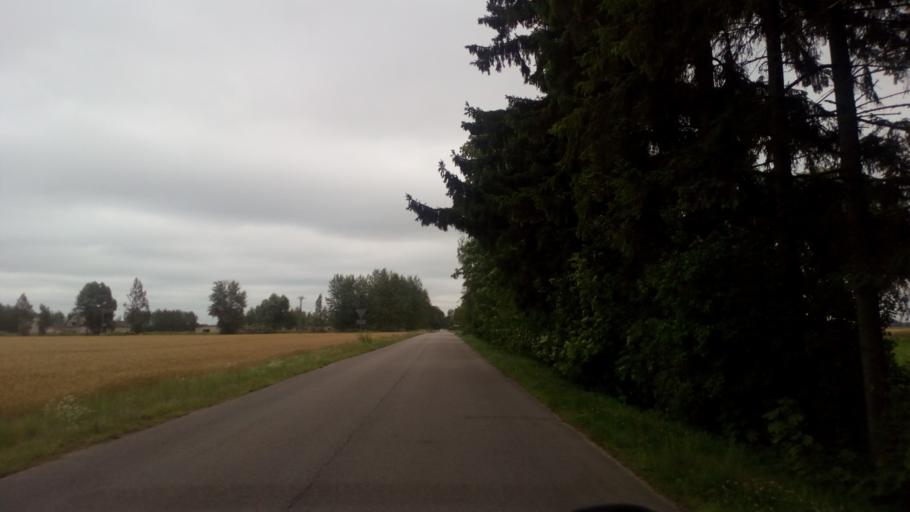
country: LV
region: Rundales
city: Pilsrundale
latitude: 56.4307
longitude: 23.9755
